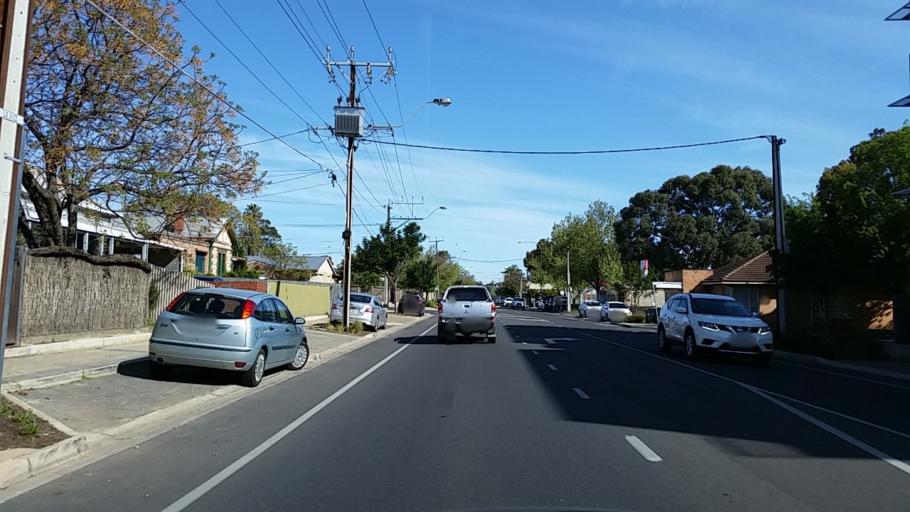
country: AU
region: South Australia
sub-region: Prospect
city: Prospect
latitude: -34.8921
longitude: 138.5853
